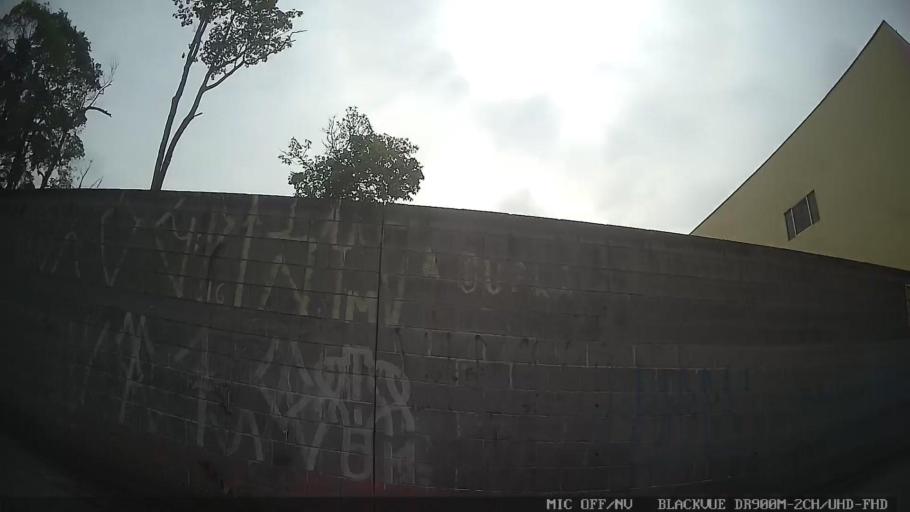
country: BR
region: Sao Paulo
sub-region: Itaquaquecetuba
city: Itaquaquecetuba
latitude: -23.5057
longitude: -46.3482
